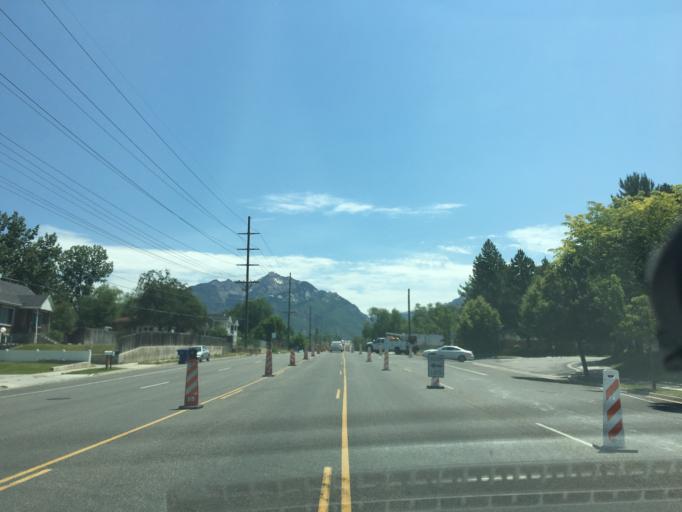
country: US
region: Utah
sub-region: Salt Lake County
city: White City
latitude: 40.5806
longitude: -111.8662
